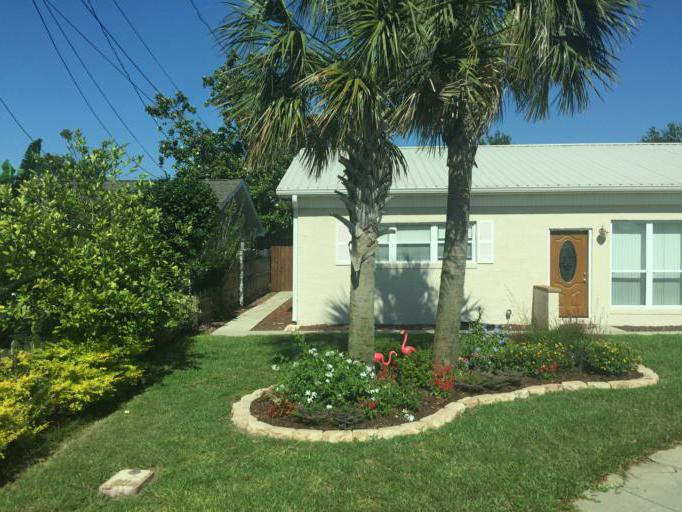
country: US
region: Florida
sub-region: Bay County
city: Panama City Beach
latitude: 30.2045
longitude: -85.8439
